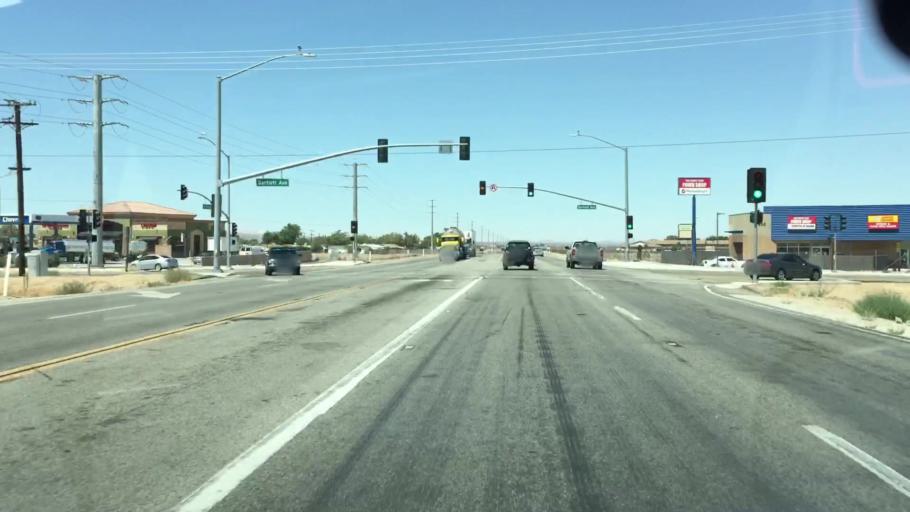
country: US
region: California
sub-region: San Bernardino County
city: Adelanto
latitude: 34.5787
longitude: -117.4118
